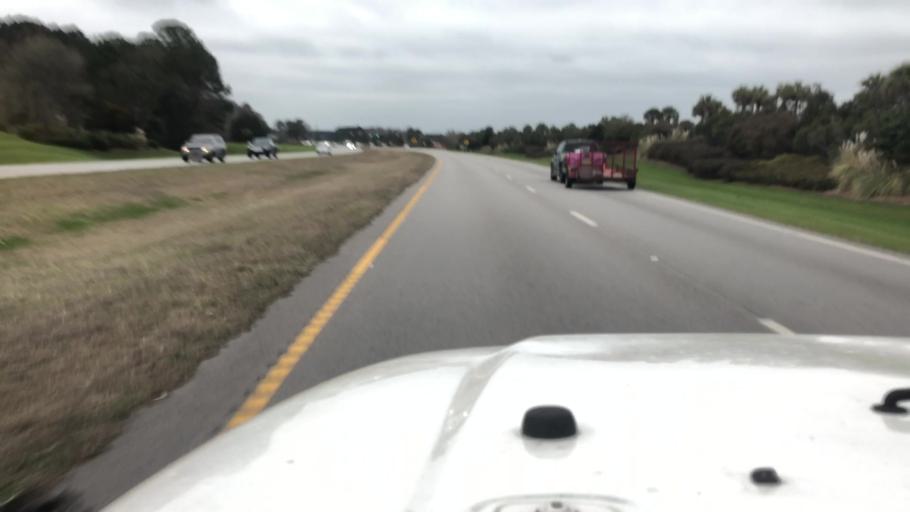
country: US
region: South Carolina
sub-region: Beaufort County
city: Bluffton
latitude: 32.3001
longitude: -80.9516
